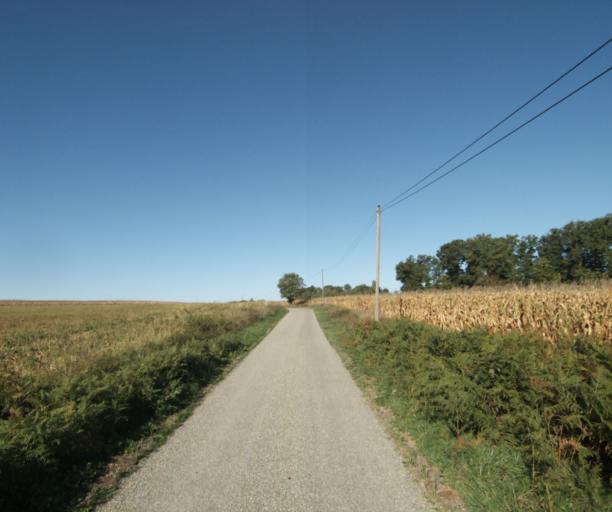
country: FR
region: Midi-Pyrenees
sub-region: Departement du Gers
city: Eauze
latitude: 43.8093
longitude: 0.1192
